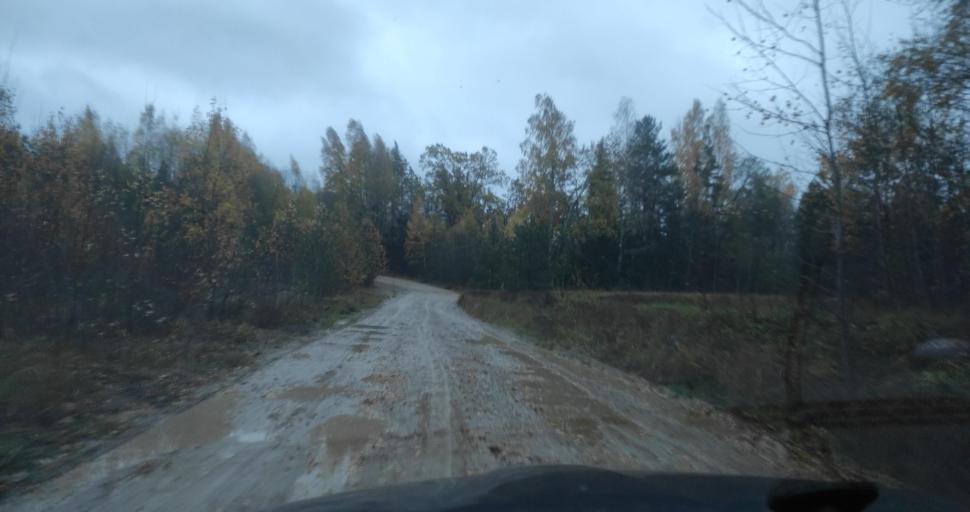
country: LV
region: Kuldigas Rajons
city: Kuldiga
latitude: 56.9060
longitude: 21.9273
